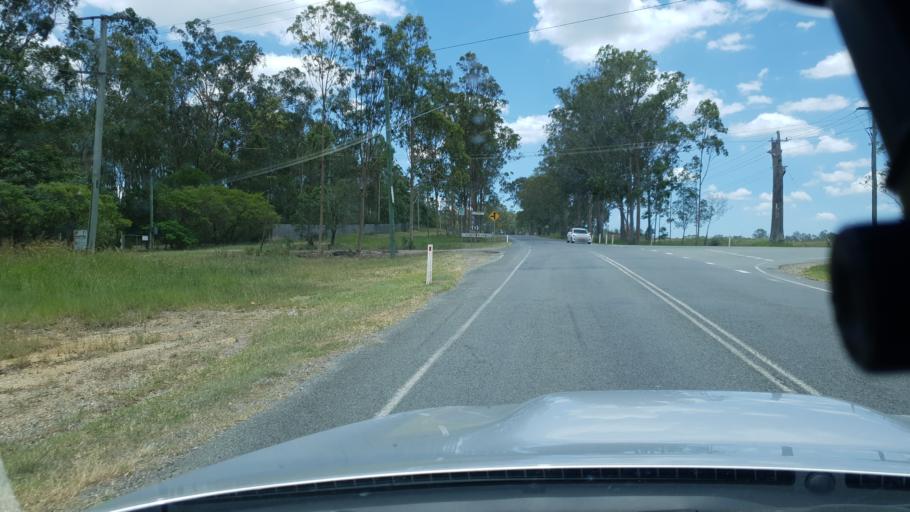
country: AU
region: Queensland
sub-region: Logan
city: North Maclean
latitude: -27.7443
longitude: 152.9854
